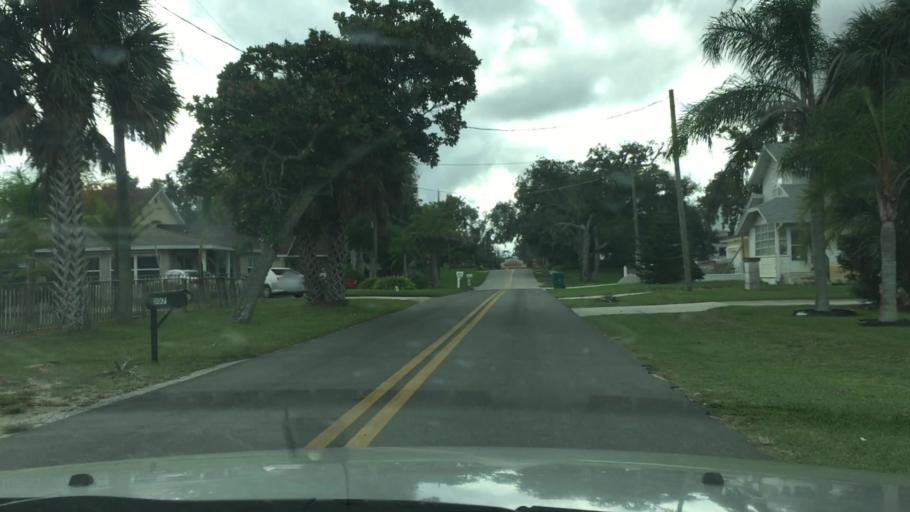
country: US
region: Florida
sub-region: Volusia County
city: Holly Hill
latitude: 29.2392
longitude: -81.0334
